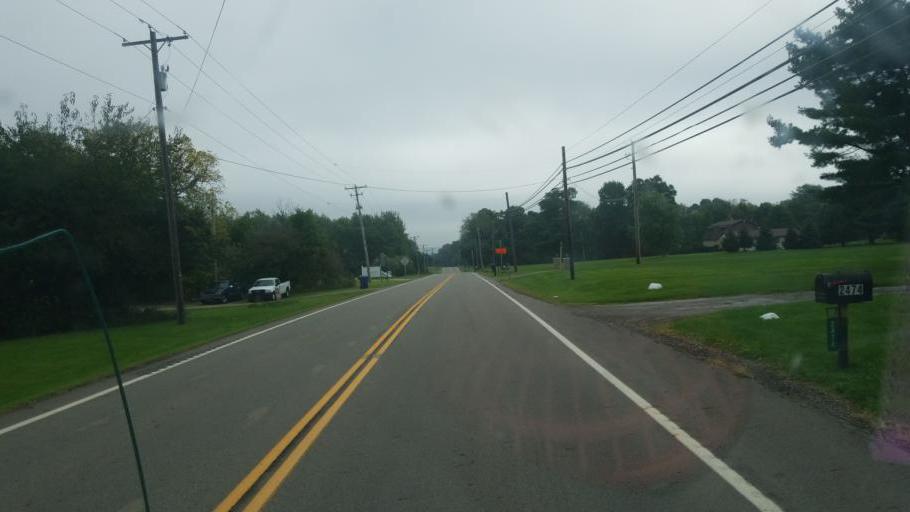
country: US
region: Ohio
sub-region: Richland County
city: Lincoln Heights
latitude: 40.7665
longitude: -82.4228
